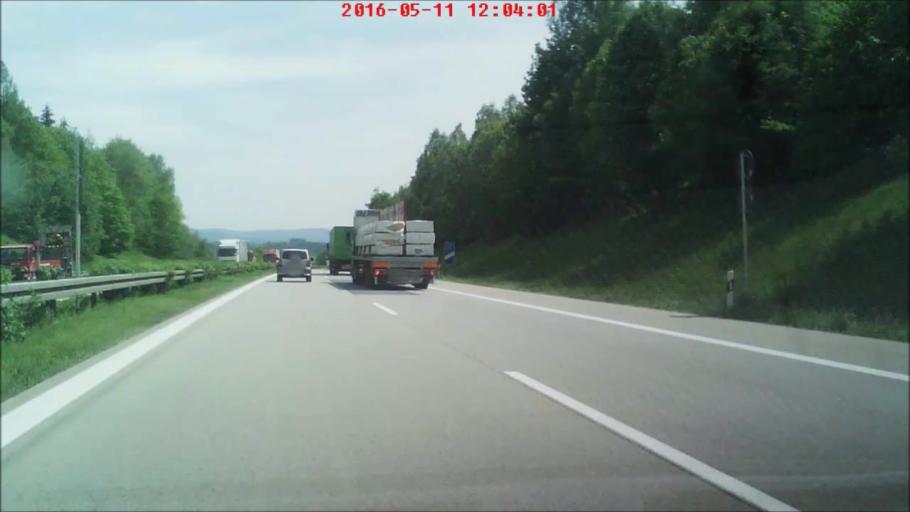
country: DE
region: Bavaria
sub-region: Lower Bavaria
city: Niederwinkling
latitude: 48.9020
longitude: 12.7937
